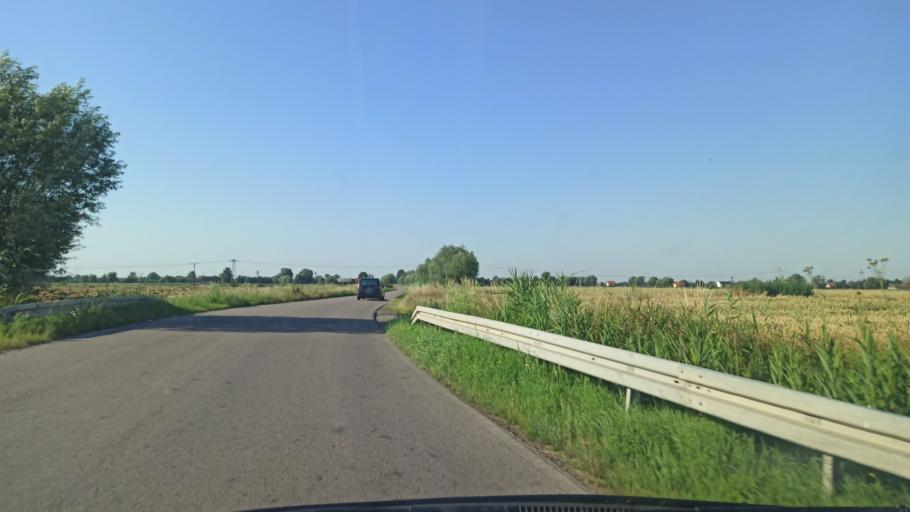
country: PL
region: Warmian-Masurian Voivodeship
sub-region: Powiat elblaski
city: Elblag
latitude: 54.1815
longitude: 19.3324
